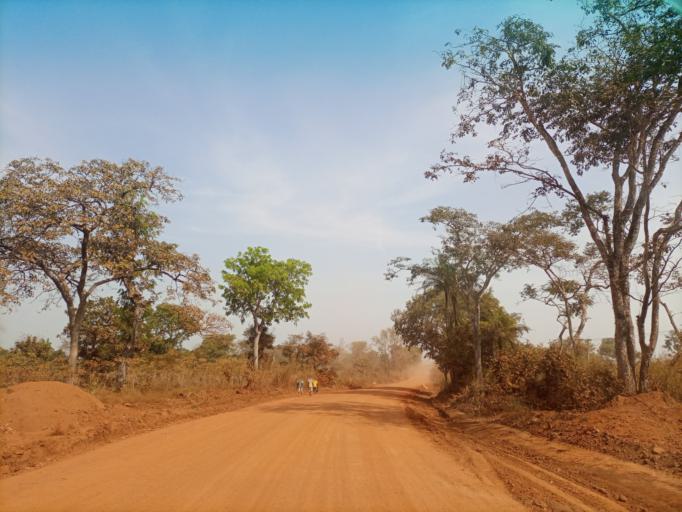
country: NG
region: Enugu
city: Eha Amufu
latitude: 6.6691
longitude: 7.7444
